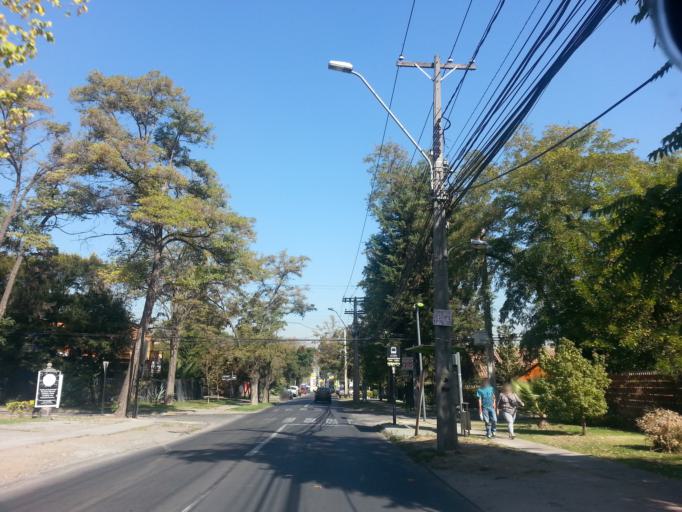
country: CL
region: Santiago Metropolitan
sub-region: Provincia de Santiago
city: Villa Presidente Frei, Nunoa, Santiago, Chile
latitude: -33.4484
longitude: -70.5438
